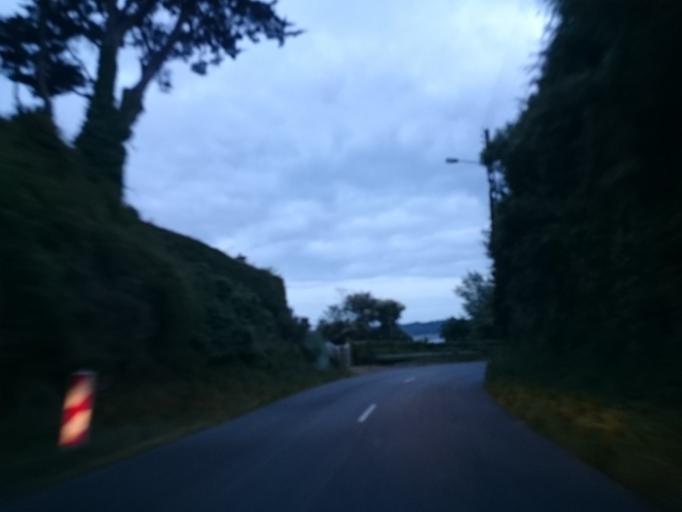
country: FR
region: Brittany
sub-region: Departement des Cotes-d'Armor
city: Perros-Guirec
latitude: 48.8169
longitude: -3.4317
